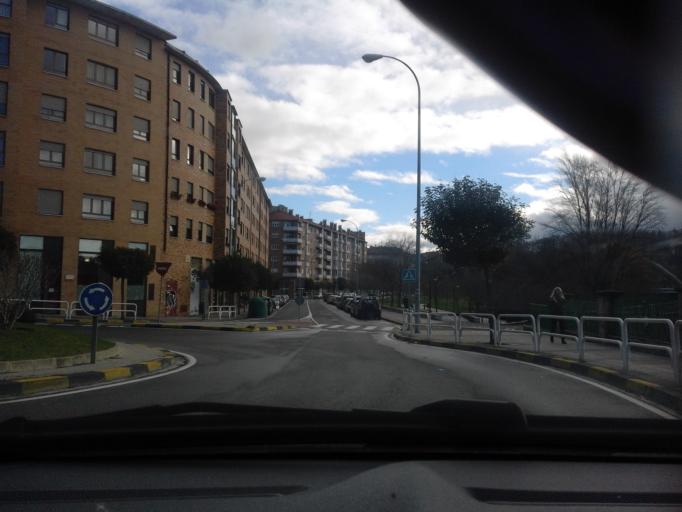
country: ES
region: Navarre
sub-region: Provincia de Navarra
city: Berriozar
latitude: 42.8247
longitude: -1.6560
